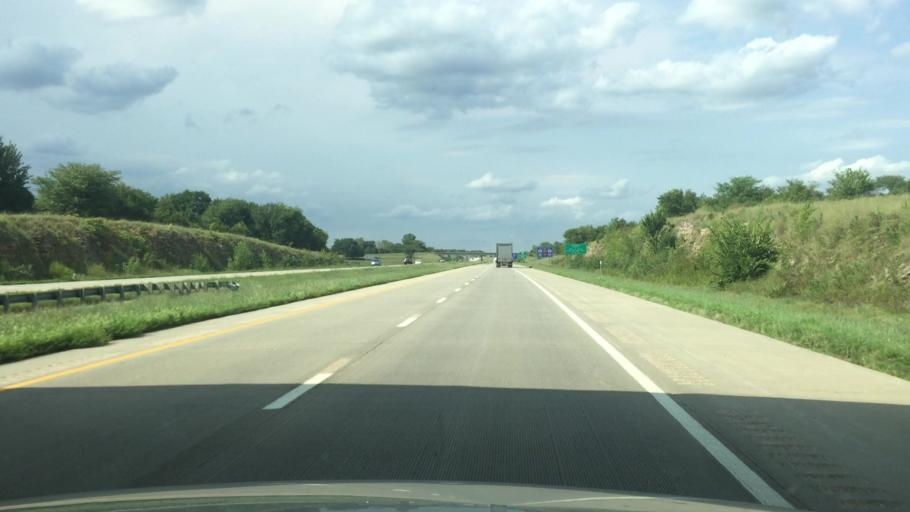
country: US
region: Kansas
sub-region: Miami County
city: Louisburg
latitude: 38.6066
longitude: -94.6940
